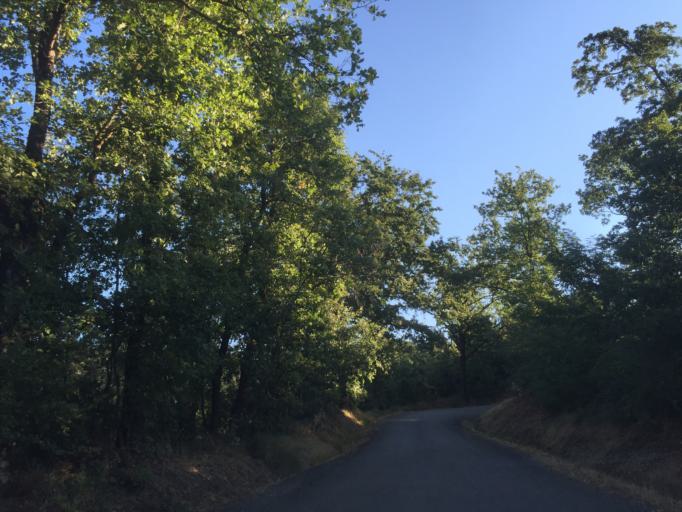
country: IT
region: Tuscany
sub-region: Provincia di Pistoia
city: Pistoia
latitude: 43.9472
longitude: 10.9575
